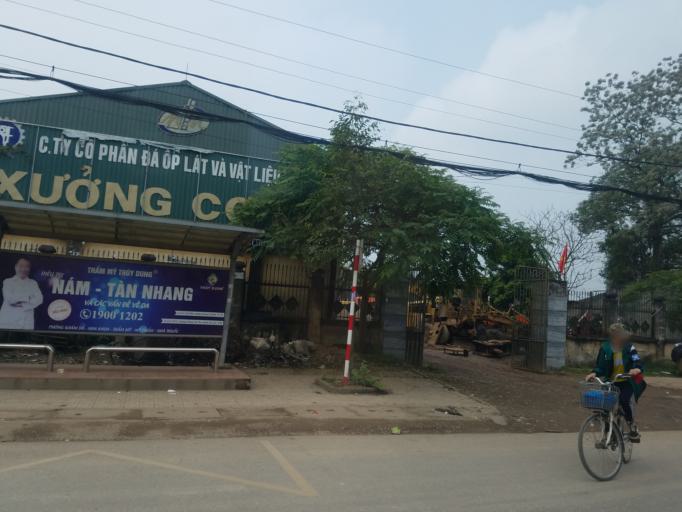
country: VN
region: Thai Nguyen
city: Chua Hang
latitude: 21.6184
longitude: 105.8388
